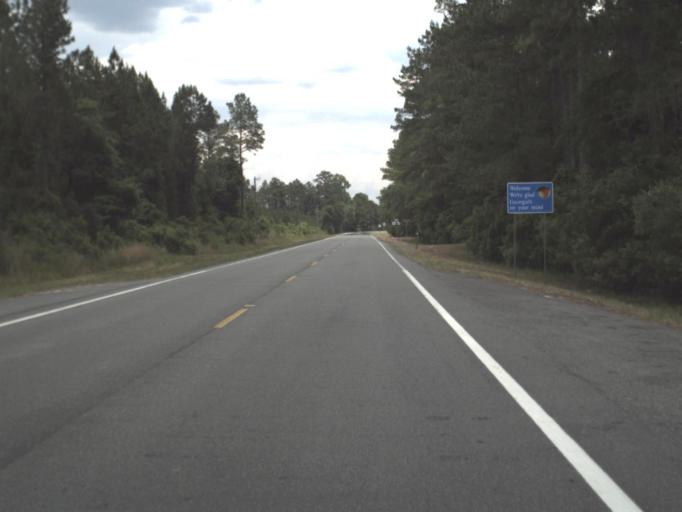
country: US
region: Florida
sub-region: Hamilton County
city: Jasper
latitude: 30.5974
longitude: -82.6702
